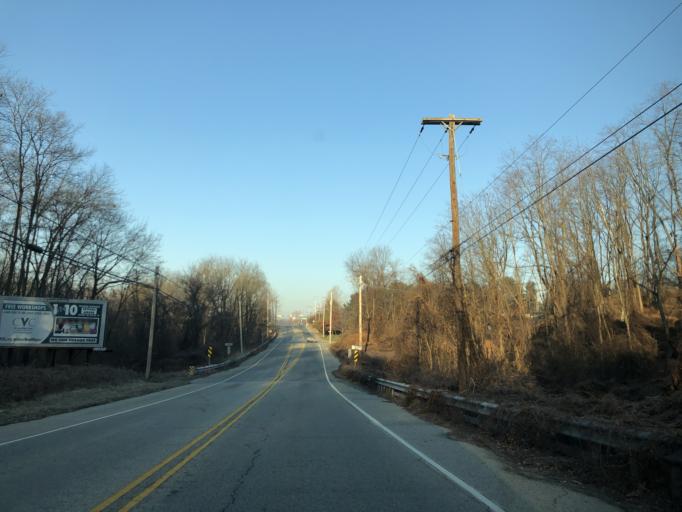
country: US
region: Pennsylvania
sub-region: Chester County
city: West Chester
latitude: 39.9627
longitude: -75.6240
